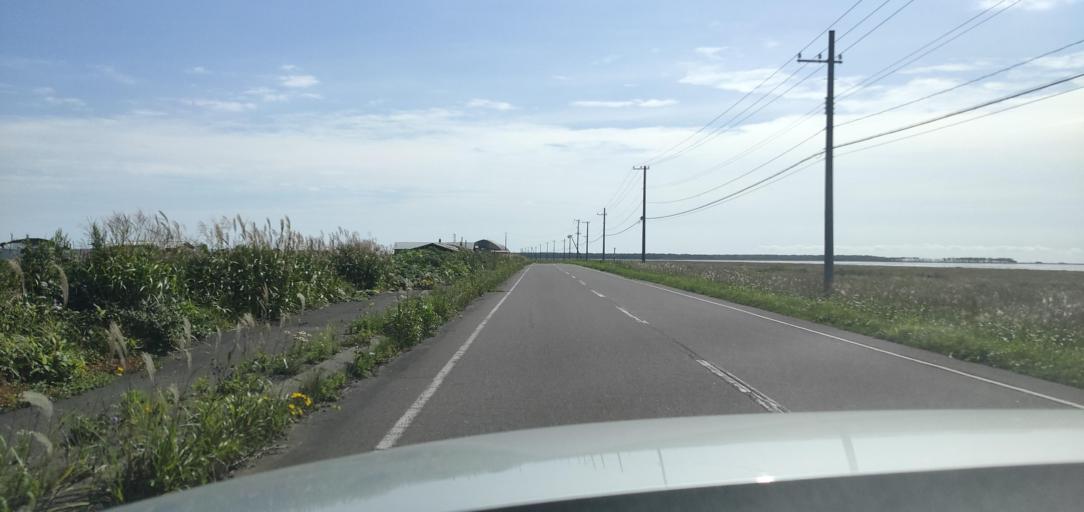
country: JP
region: Hokkaido
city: Shibetsu
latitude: 43.6170
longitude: 145.2371
